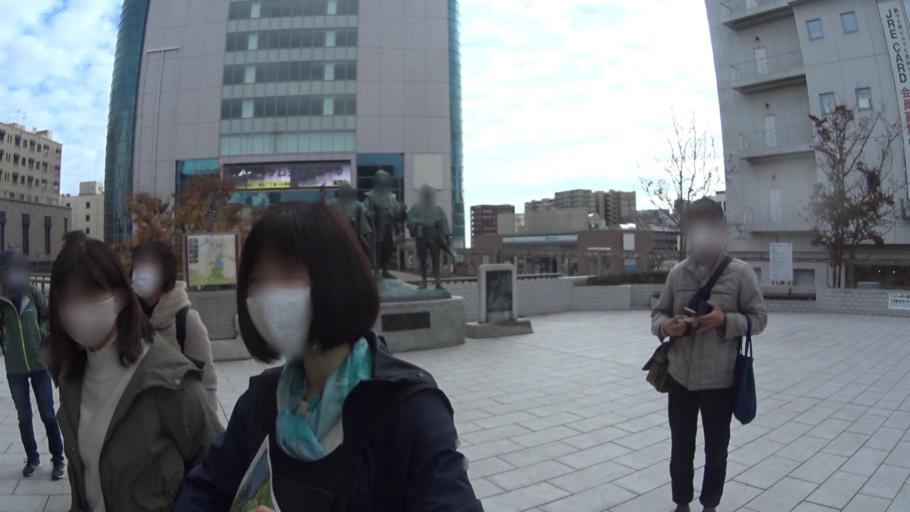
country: JP
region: Ibaraki
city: Mito-shi
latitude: 36.3727
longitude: 140.4775
